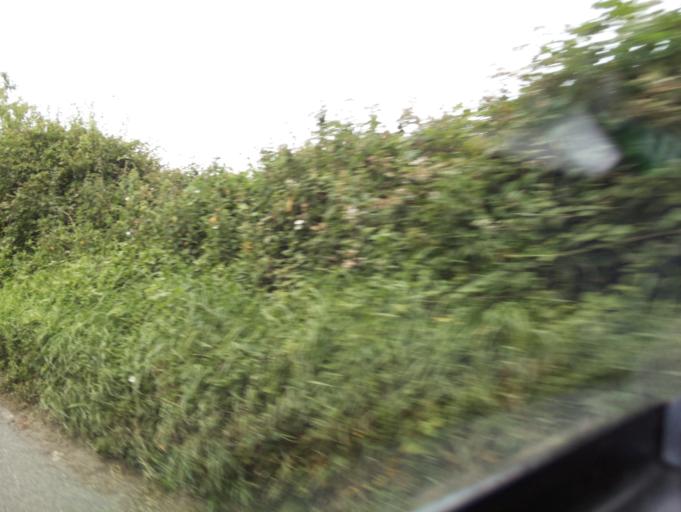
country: GB
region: England
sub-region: Somerset
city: Street
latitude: 51.1111
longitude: -2.7027
